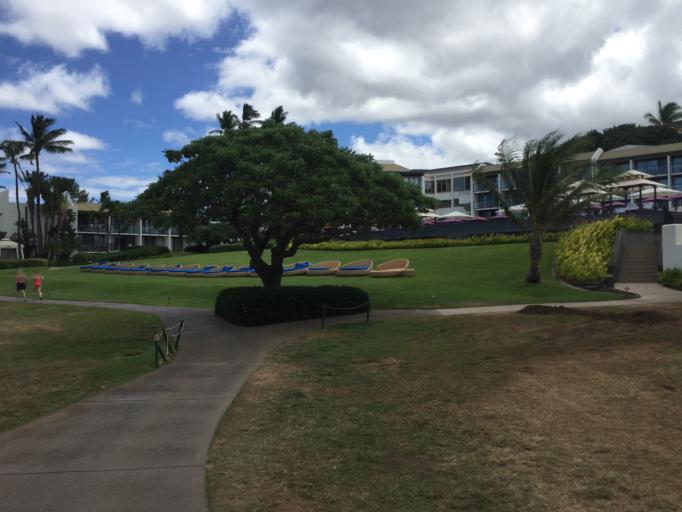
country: US
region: Hawaii
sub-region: Maui County
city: Kihei
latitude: 20.6867
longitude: -156.4443
